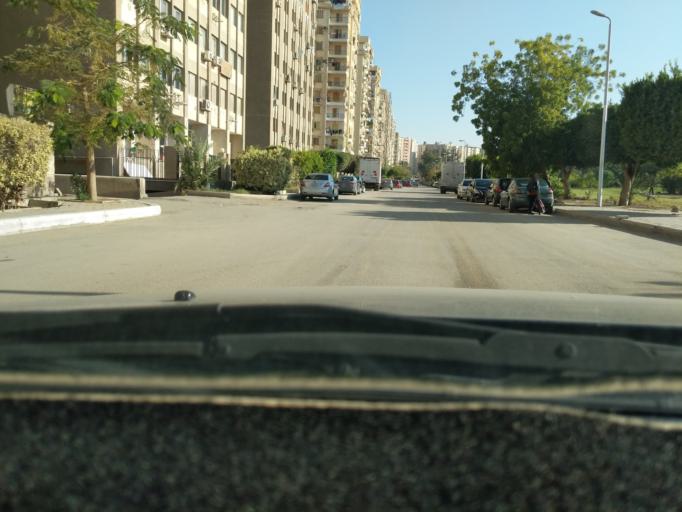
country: EG
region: Al Jizah
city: Al Hawamidiyah
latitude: 29.9618
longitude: 31.3167
